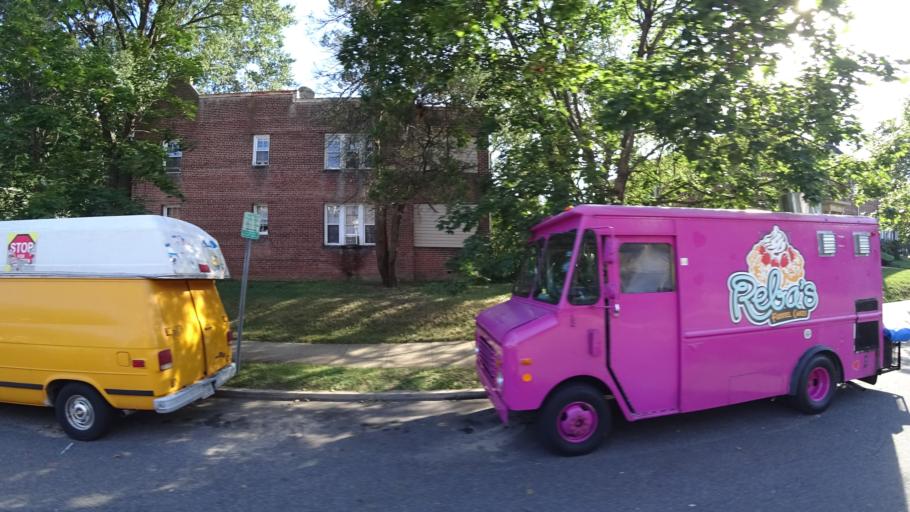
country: US
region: Maryland
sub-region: Prince George's County
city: Chillum
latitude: 38.9394
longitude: -76.9942
